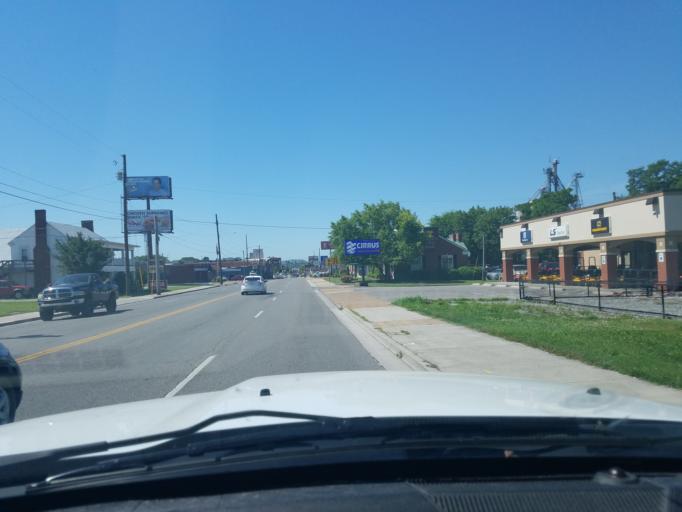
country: US
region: Tennessee
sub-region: Wilson County
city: Lebanon
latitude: 36.2110
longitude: -86.2907
